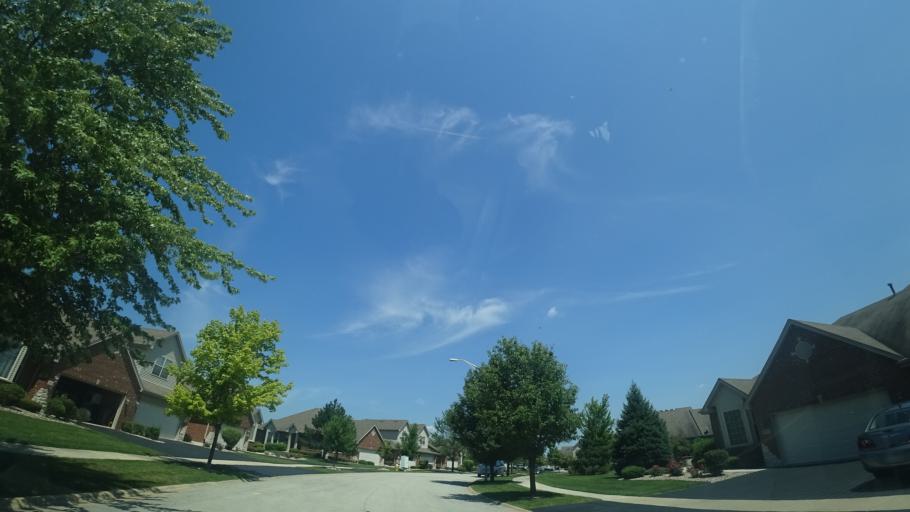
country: US
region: Illinois
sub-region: Will County
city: Mokena
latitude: 41.5612
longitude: -87.9036
